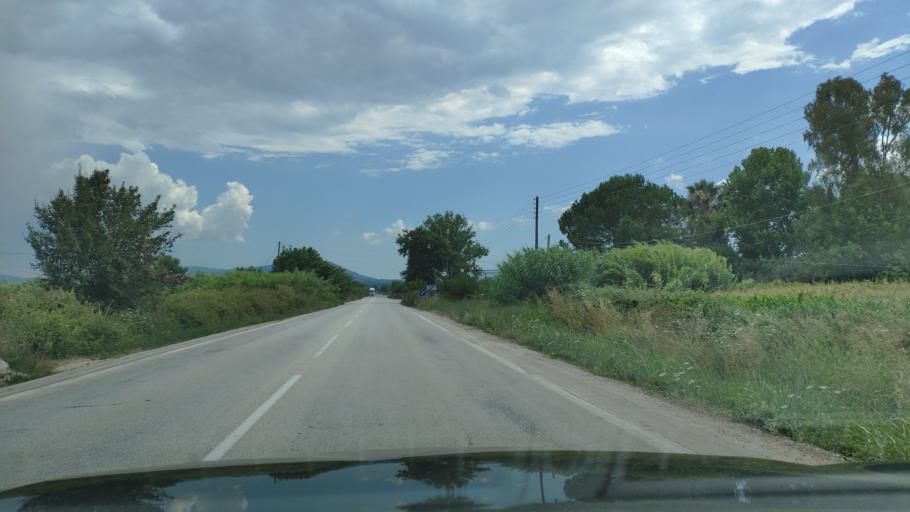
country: GR
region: West Greece
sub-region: Nomos Aitolias kai Akarnanias
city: Krikellos
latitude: 38.9409
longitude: 21.1768
